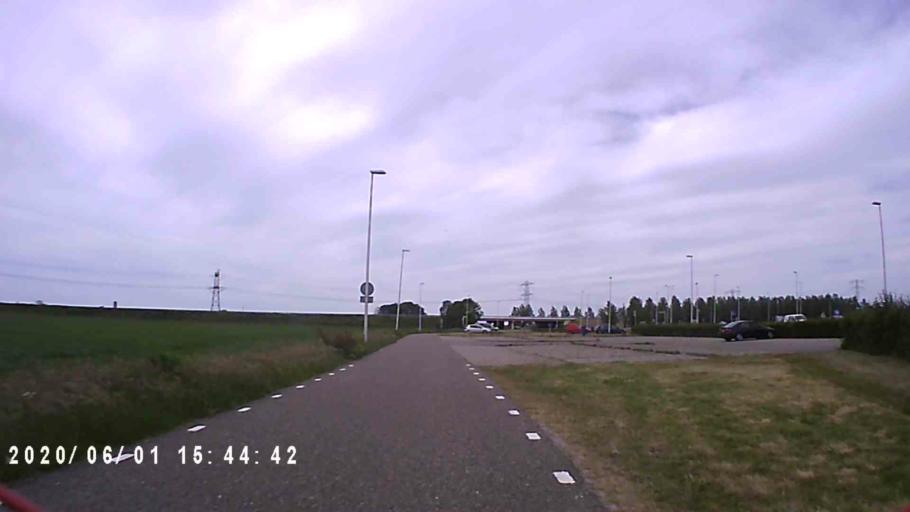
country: NL
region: Friesland
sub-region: Gemeente Boarnsterhim
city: Wergea
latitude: 53.1642
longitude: 5.8295
